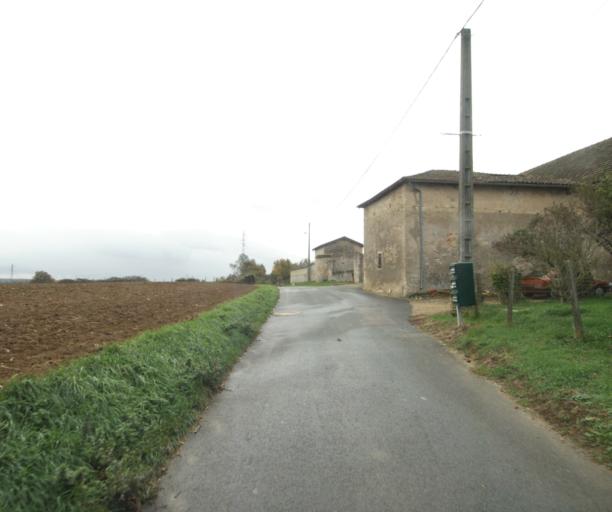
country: FR
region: Rhone-Alpes
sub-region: Departement de l'Ain
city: Pont-de-Vaux
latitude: 46.4682
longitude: 4.8855
